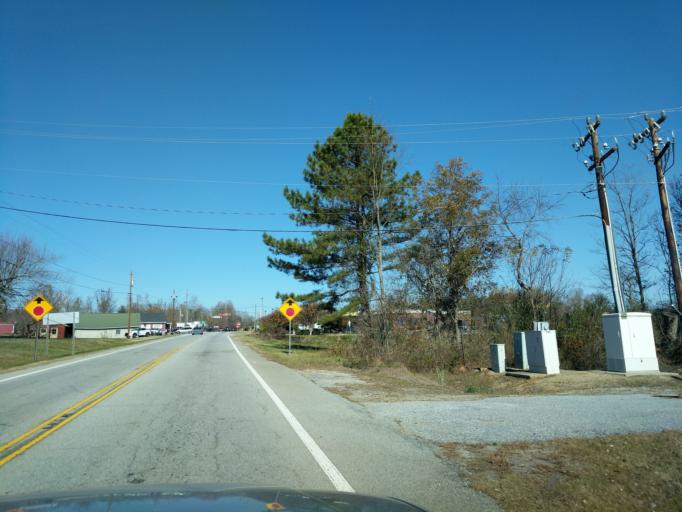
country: US
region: South Carolina
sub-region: Spartanburg County
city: Landrum
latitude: 35.1113
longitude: -82.2253
